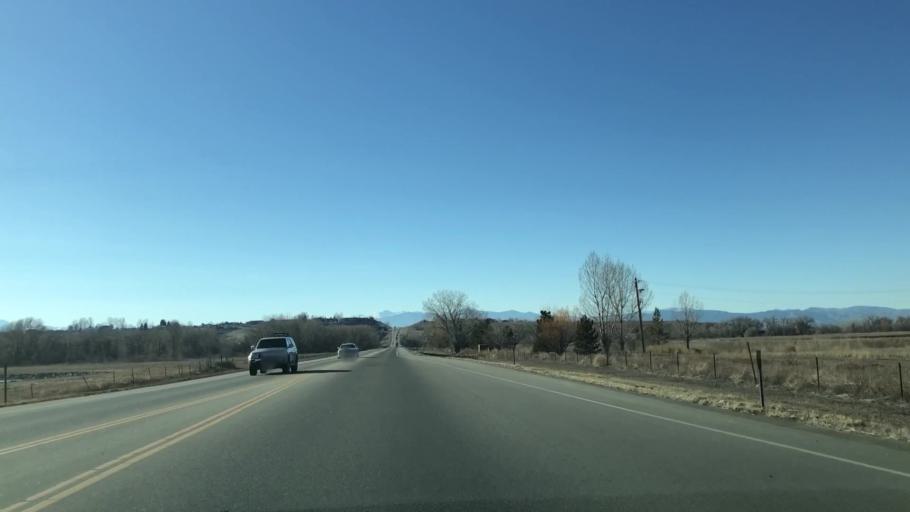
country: US
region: Colorado
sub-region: Weld County
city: Windsor
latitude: 40.4794
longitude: -104.9470
